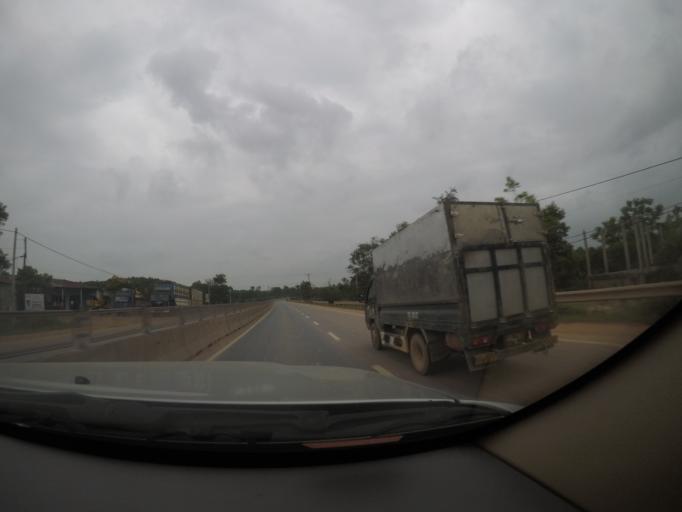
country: VN
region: Thua Thien-Hue
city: Phong Dien
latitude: 16.6170
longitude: 107.3109
